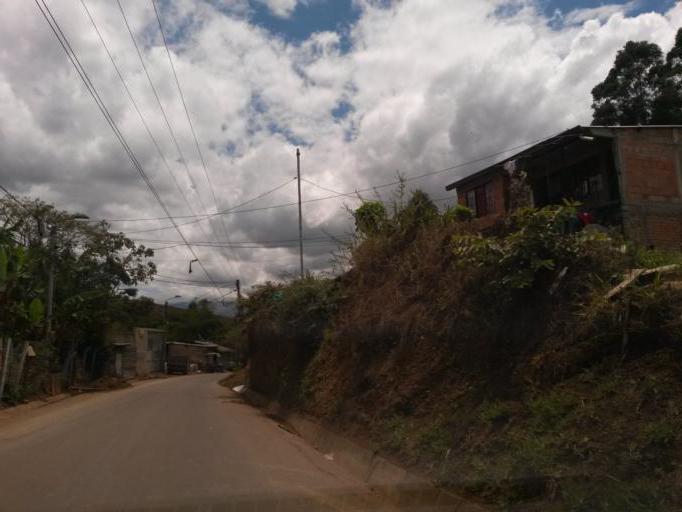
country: CO
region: Cauca
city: Popayan
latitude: 2.4790
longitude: -76.5669
